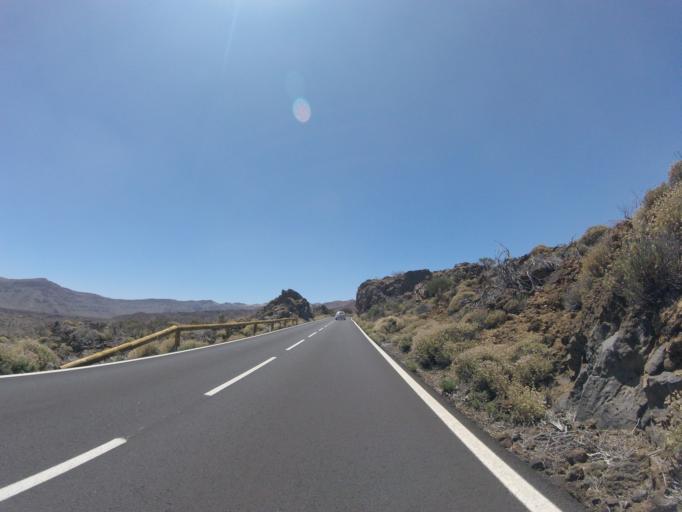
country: ES
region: Canary Islands
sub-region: Provincia de Santa Cruz de Tenerife
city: Los Realejos
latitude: 28.2871
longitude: -16.5650
